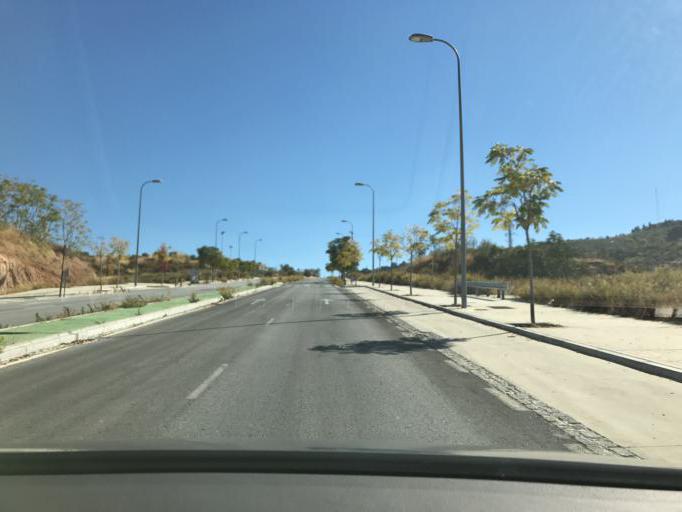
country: ES
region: Andalusia
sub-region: Provincia de Granada
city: Jun
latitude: 37.2018
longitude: -3.5930
